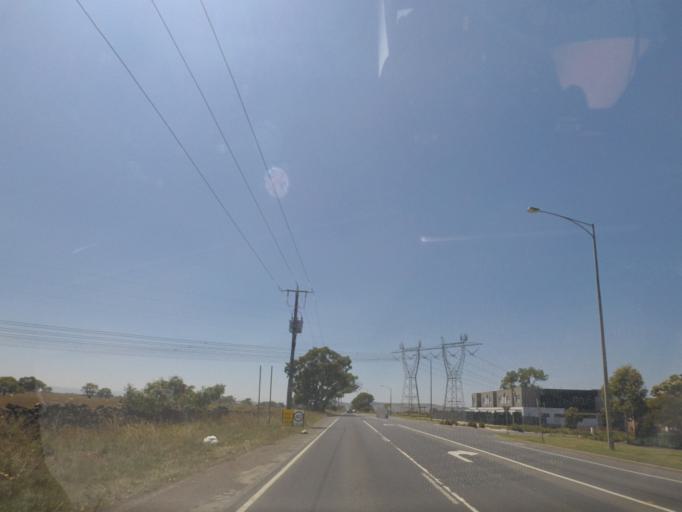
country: AU
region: Victoria
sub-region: Whittlesea
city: Epping
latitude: -37.6067
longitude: 145.0140
